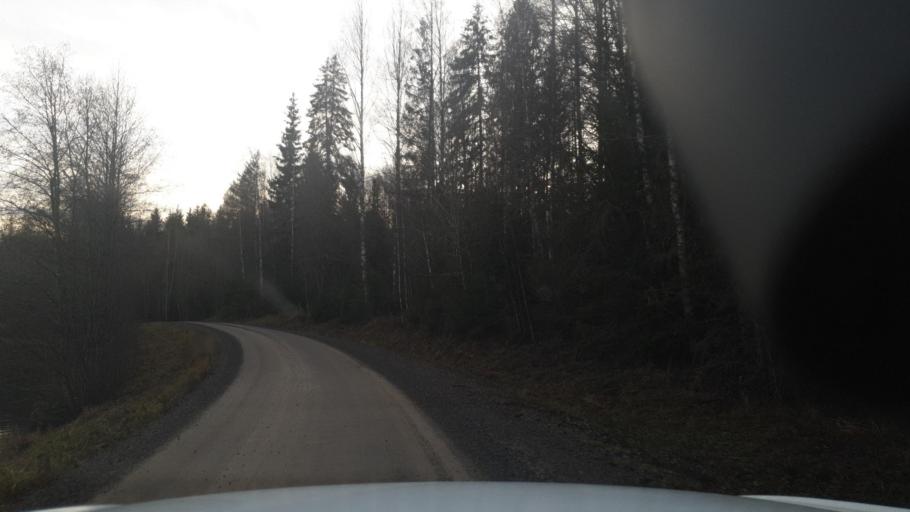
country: NO
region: Hedmark
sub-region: Eidskog
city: Skotterud
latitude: 59.8832
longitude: 11.9765
